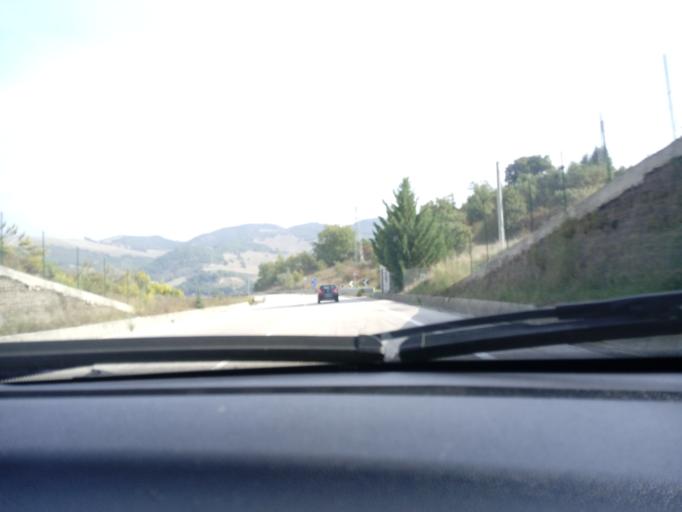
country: IT
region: Molise
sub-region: Provincia di Campobasso
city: Gambatesa
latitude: 41.5307
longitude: 14.8799
